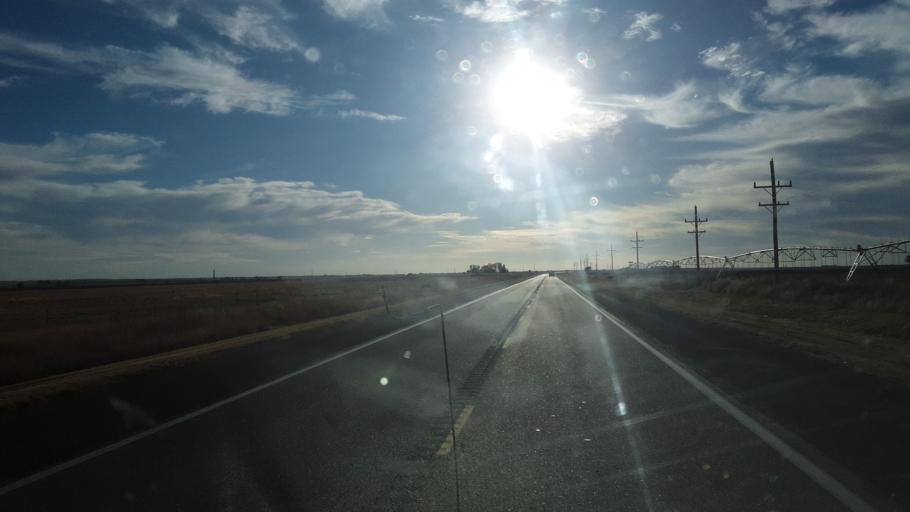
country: US
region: Kansas
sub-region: Kearny County
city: Lakin
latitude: 37.9647
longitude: -101.2105
